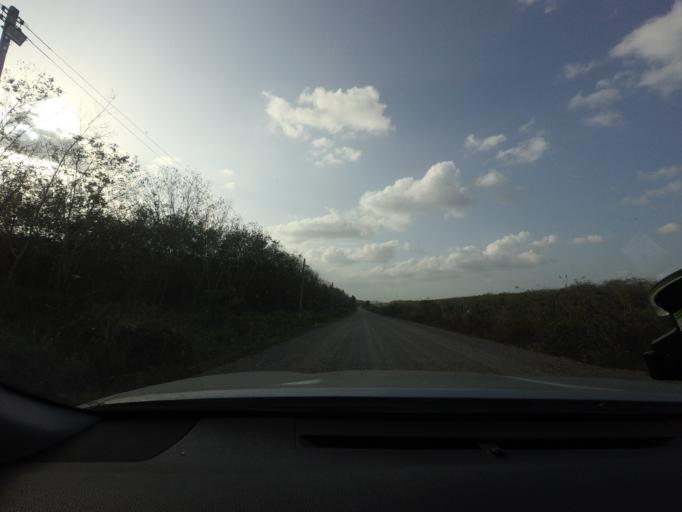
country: TH
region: Pattani
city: Mae Lan
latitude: 6.6175
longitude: 101.2541
